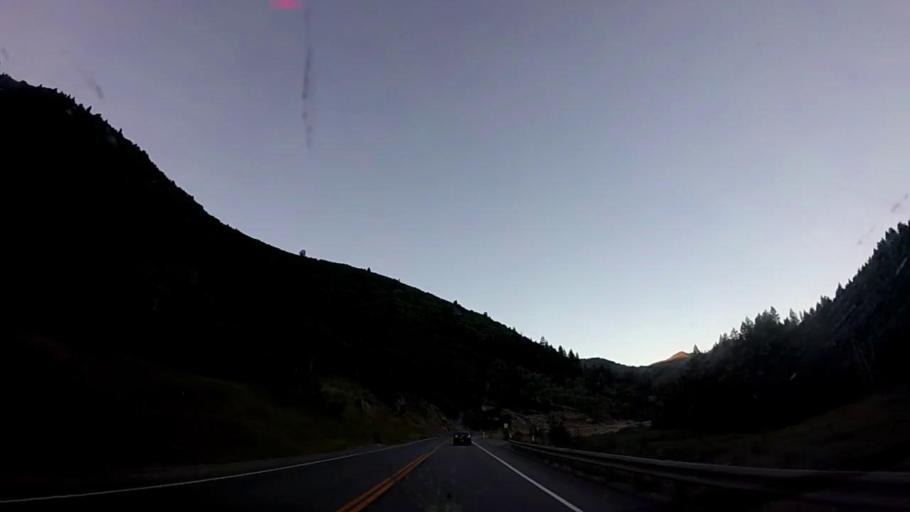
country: US
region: Utah
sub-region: Summit County
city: Summit Park
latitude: 40.6443
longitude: -111.6742
